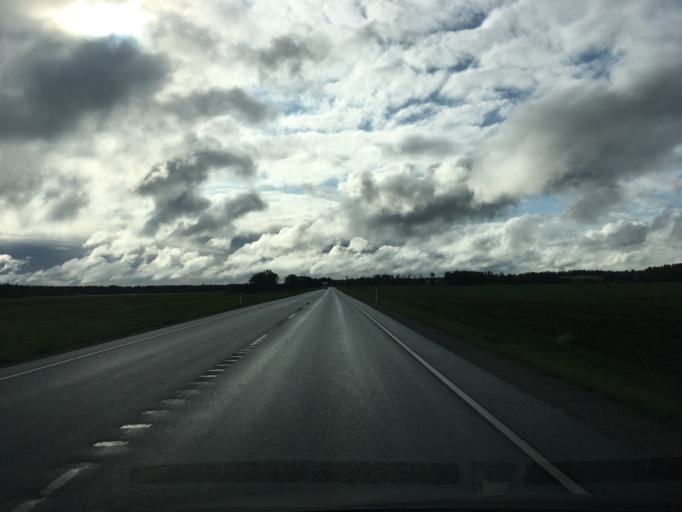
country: EE
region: Laeaene-Virumaa
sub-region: Someru vald
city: Someru
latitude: 59.3541
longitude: 26.3974
